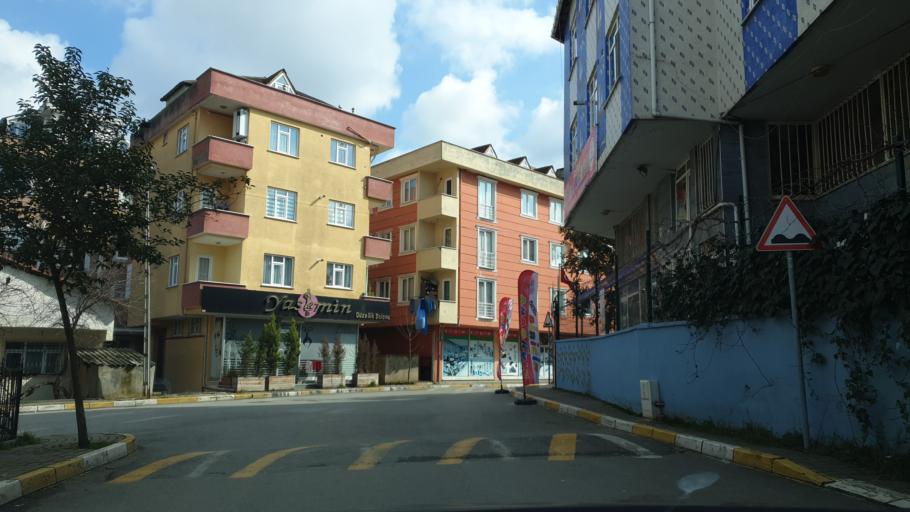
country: TR
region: Istanbul
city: Icmeler
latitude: 40.8670
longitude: 29.3056
